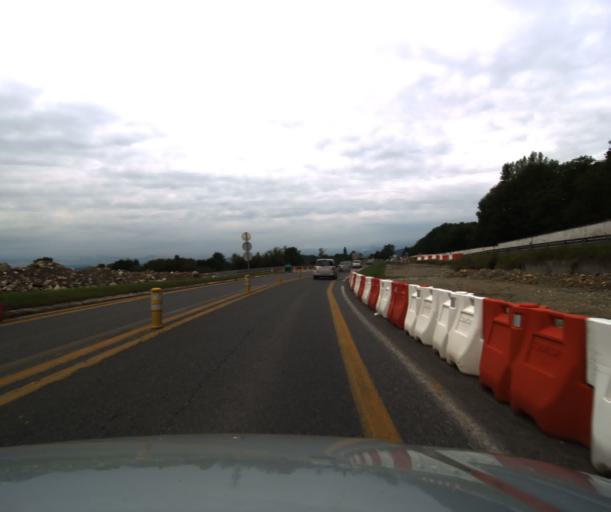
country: FR
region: Midi-Pyrenees
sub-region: Departement des Hautes-Pyrenees
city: Juillan
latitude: 43.1824
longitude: 0.0123
